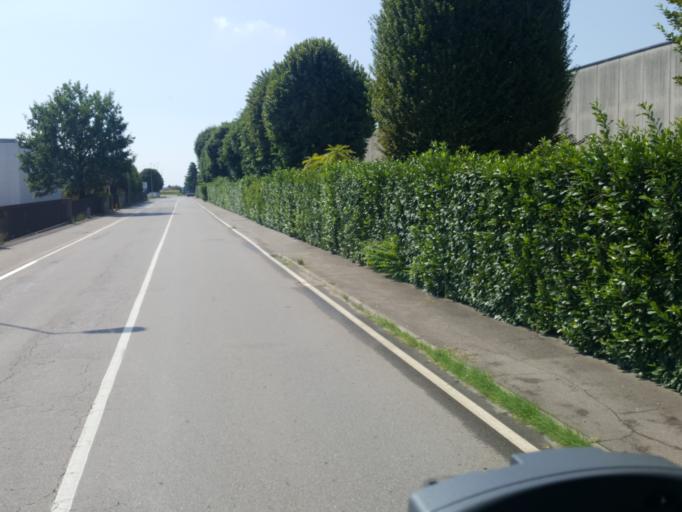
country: IT
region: Lombardy
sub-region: Provincia di Como
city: Turate
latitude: 45.6571
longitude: 9.0178
